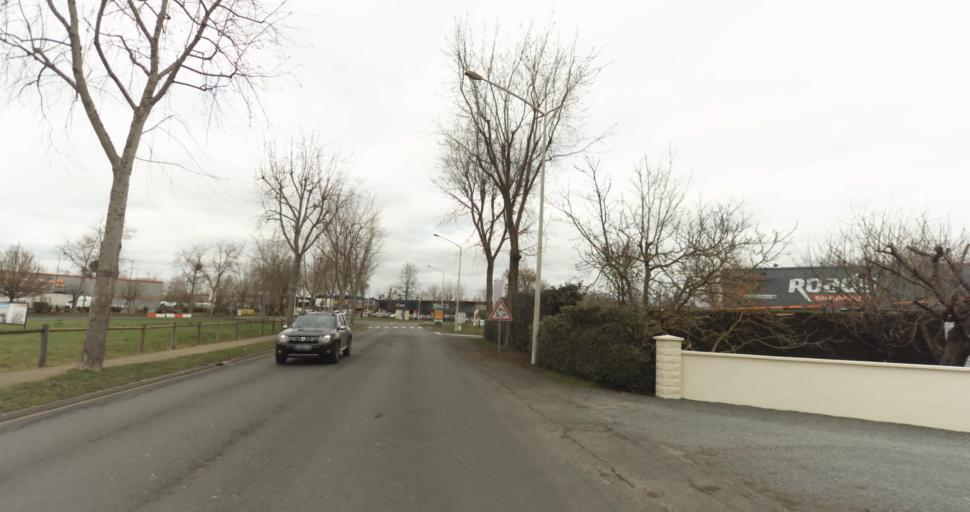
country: FR
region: Pays de la Loire
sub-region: Departement de Maine-et-Loire
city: Saumur
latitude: 47.2761
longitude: -0.0616
